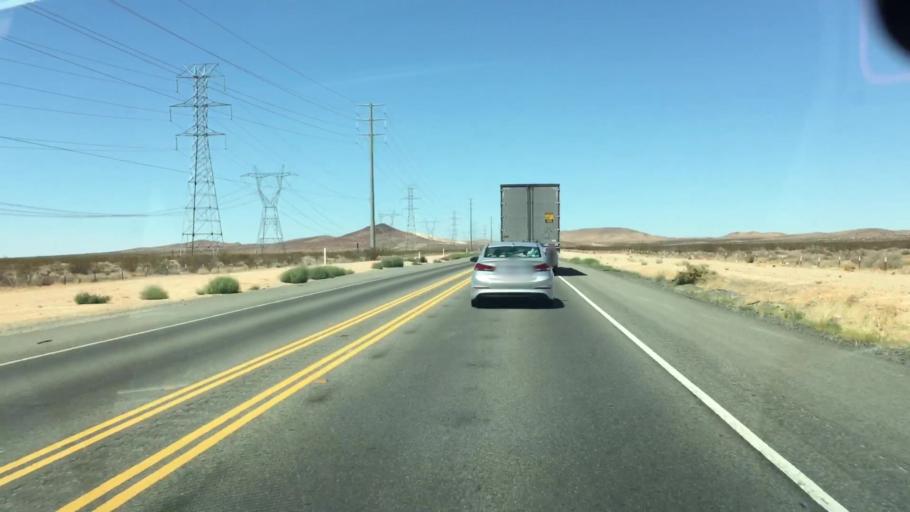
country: US
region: California
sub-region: Kern County
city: Boron
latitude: 34.8416
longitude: -117.5000
